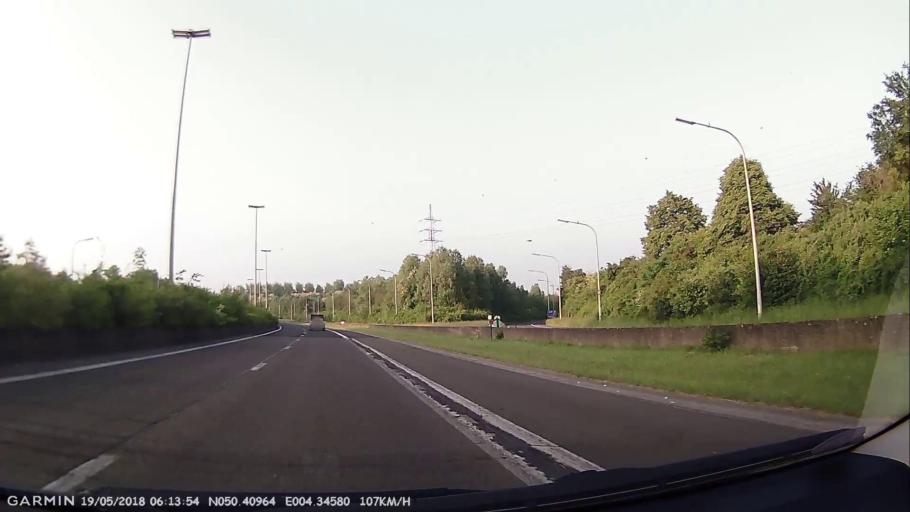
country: BE
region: Wallonia
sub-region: Province du Hainaut
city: Courcelles
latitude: 50.4095
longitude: 4.3458
